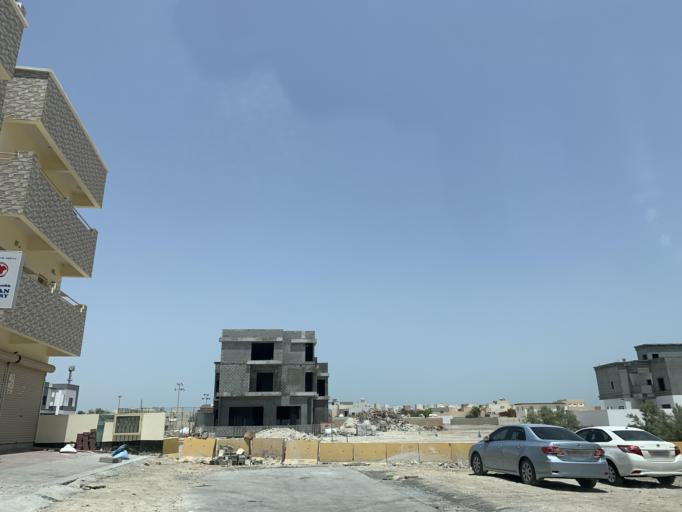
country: BH
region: Northern
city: Sitrah
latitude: 26.1431
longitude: 50.5914
